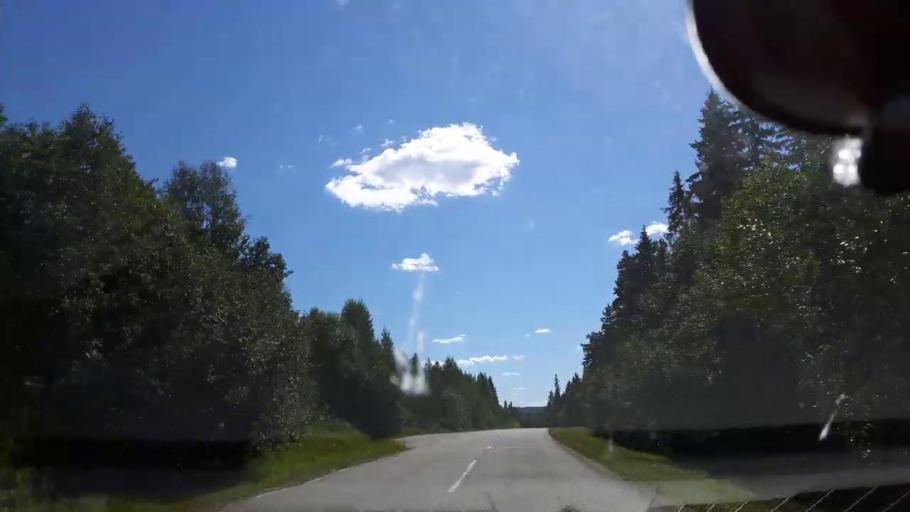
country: SE
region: Vaesternorrland
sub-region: Ange Kommun
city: Fransta
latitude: 62.7362
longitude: 16.3311
